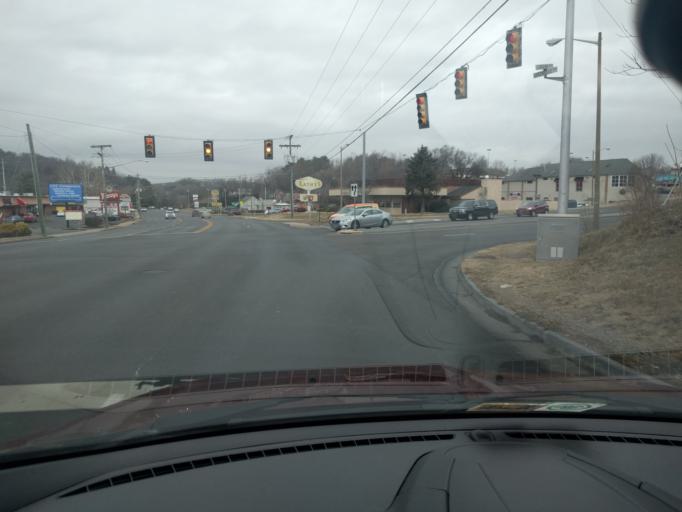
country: US
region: Virginia
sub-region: City of Staunton
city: Staunton
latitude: 38.1367
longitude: -79.0667
